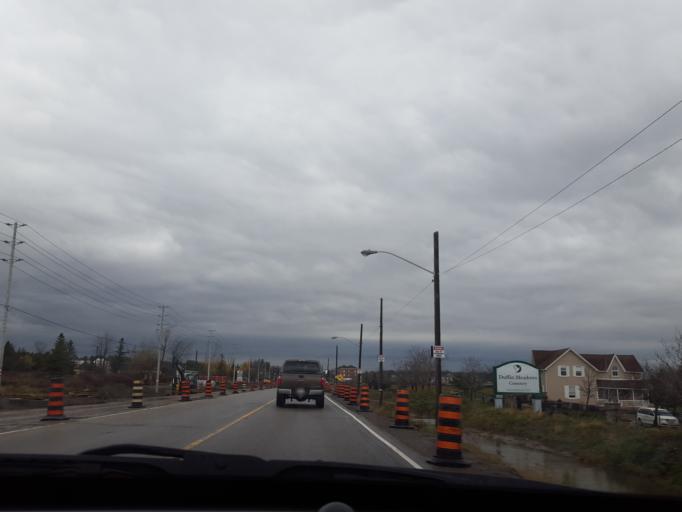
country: CA
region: Ontario
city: Ajax
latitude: 43.8714
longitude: -79.0842
